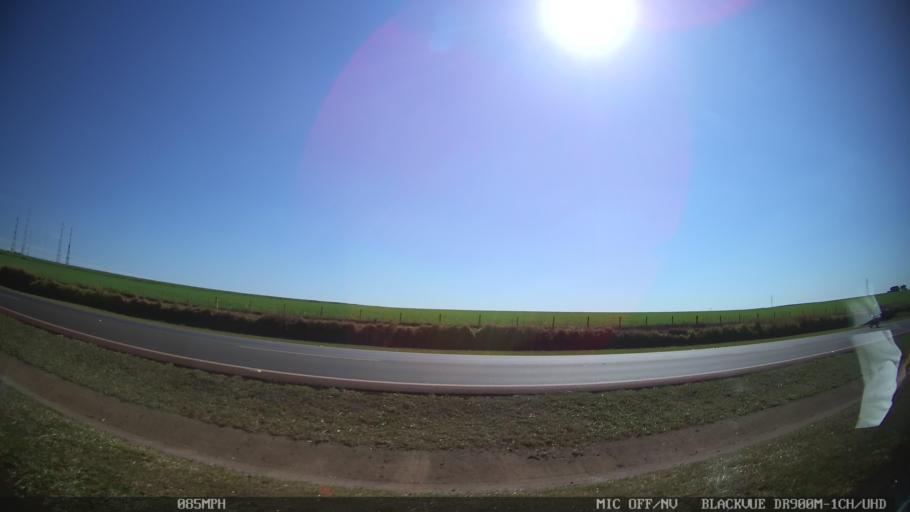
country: BR
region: Sao Paulo
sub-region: Ribeirao Preto
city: Ribeirao Preto
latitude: -21.1556
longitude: -47.8927
